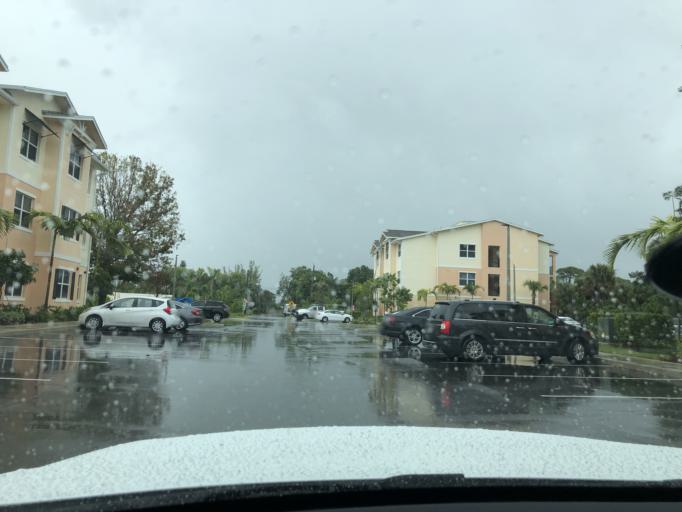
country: US
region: Florida
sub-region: Palm Beach County
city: Haverhill
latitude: 26.6968
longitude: -80.1262
